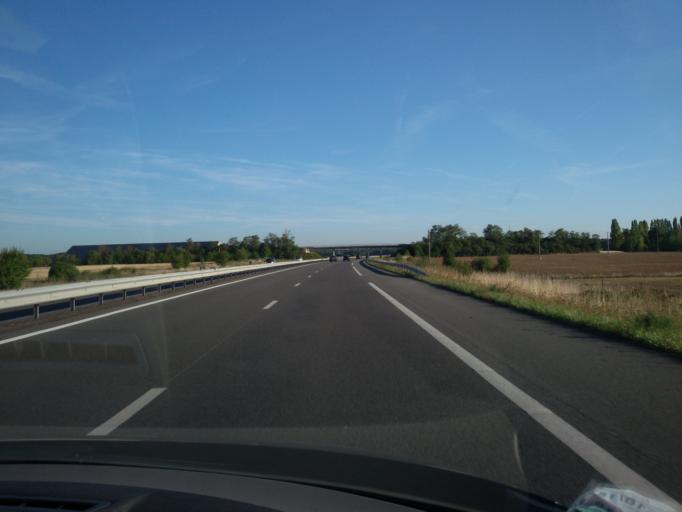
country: FR
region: Centre
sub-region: Departement du Cher
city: Levet
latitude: 46.9023
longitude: 2.4168
